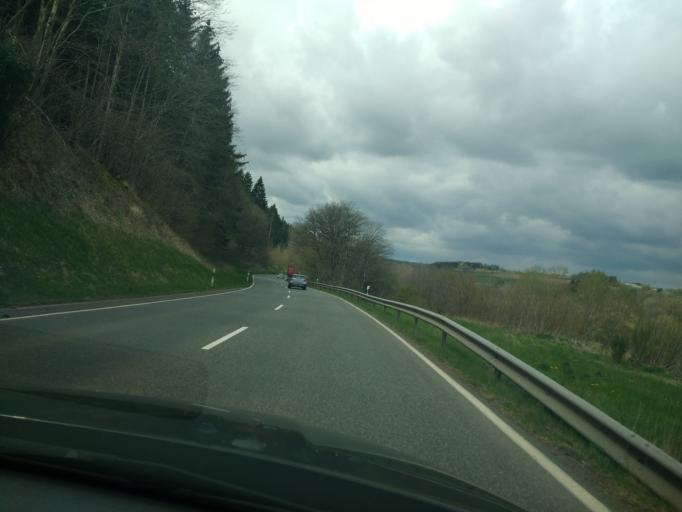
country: DE
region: Rheinland-Pfalz
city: Stadtkyll
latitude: 50.3505
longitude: 6.5567
